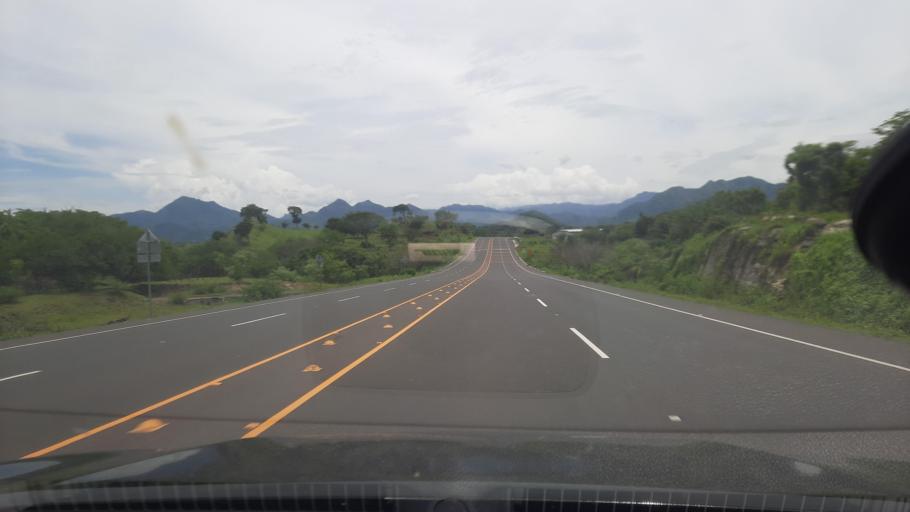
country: HN
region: Valle
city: Aramecina
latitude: 13.7903
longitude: -87.7010
